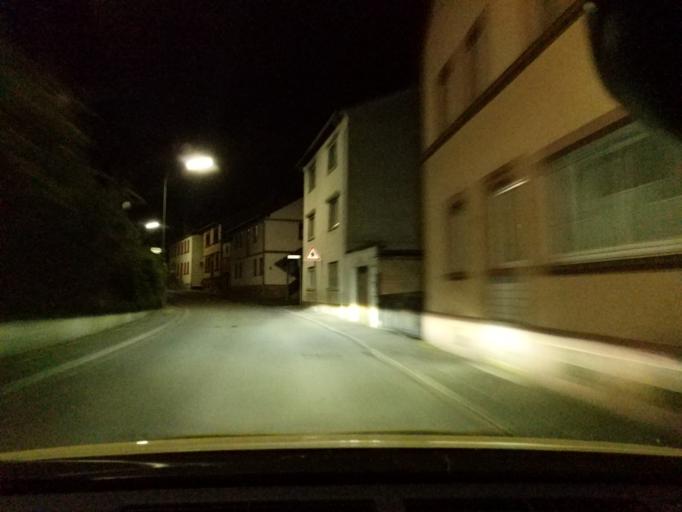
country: DE
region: Rheinland-Pfalz
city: Katzweiler
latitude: 49.4776
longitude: 7.7130
